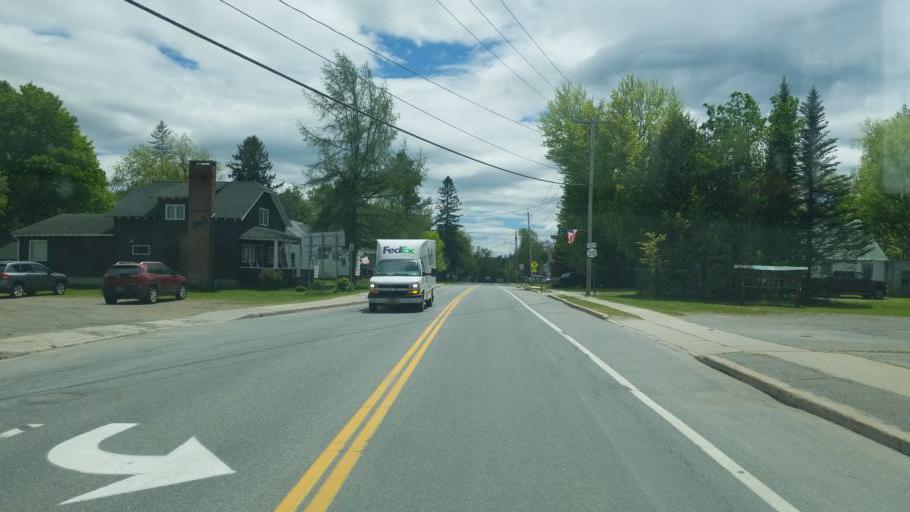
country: US
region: New York
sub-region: Hamilton County
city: Lake Pleasant
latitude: 43.7822
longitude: -74.2654
